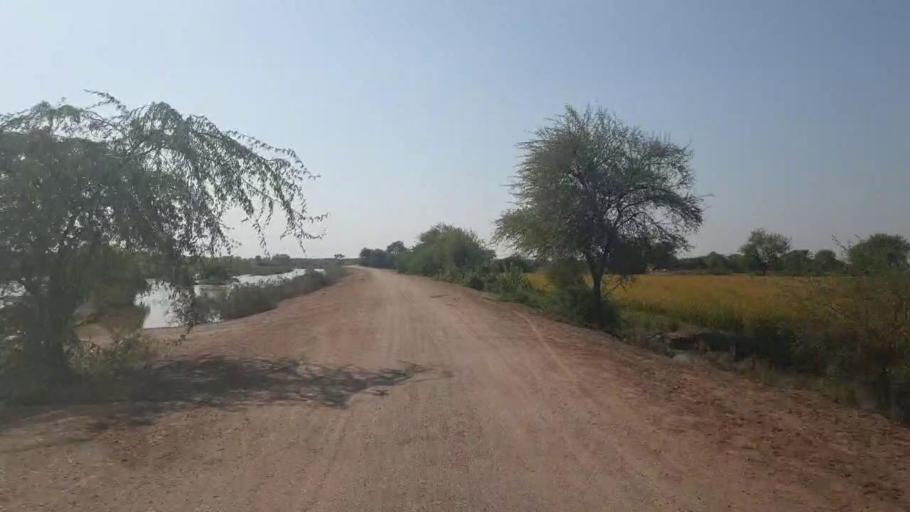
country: PK
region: Sindh
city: Badin
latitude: 24.5547
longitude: 68.8199
